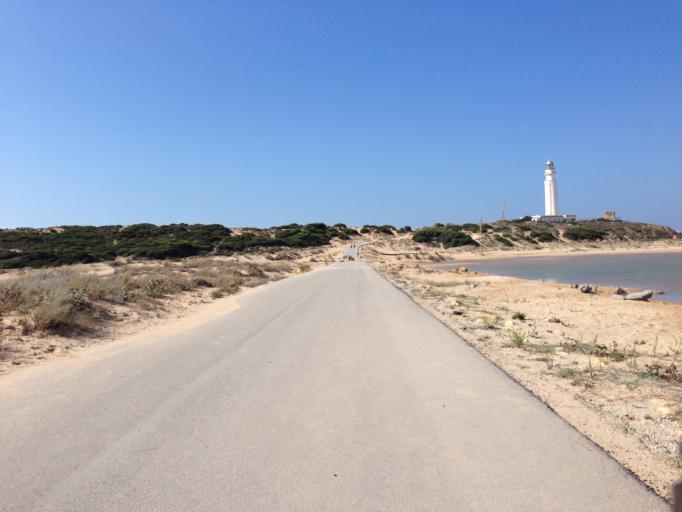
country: ES
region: Andalusia
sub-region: Provincia de Cadiz
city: Vejer de la Frontera
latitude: 36.1845
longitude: -6.0310
